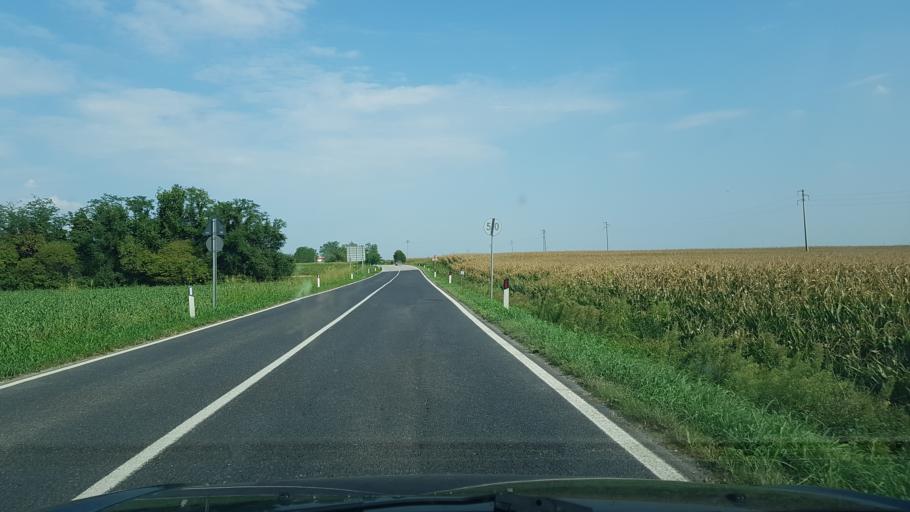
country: IT
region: Friuli Venezia Giulia
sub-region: Provincia di Udine
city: Dignano
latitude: 46.0856
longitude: 12.9515
